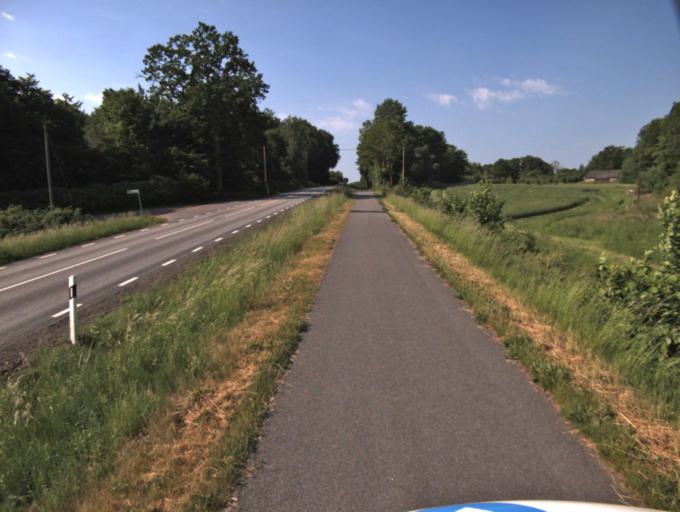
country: SE
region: Skane
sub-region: Kristianstads Kommun
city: Tollarp
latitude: 56.1581
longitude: 14.2703
